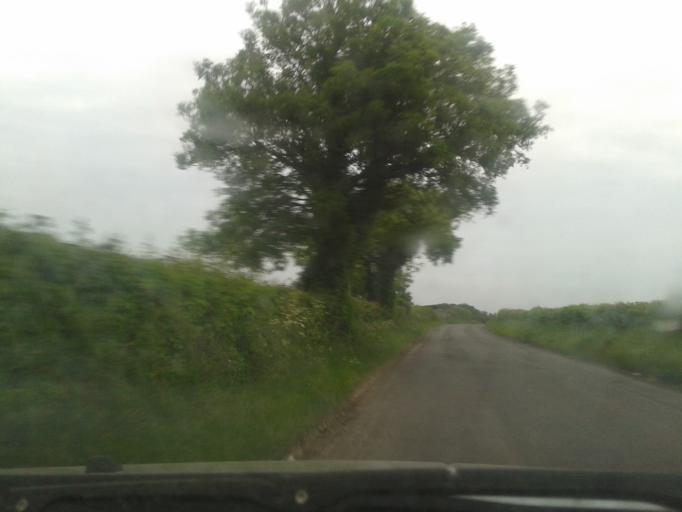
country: IE
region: Leinster
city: Ballymun
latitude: 53.4334
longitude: -6.2646
